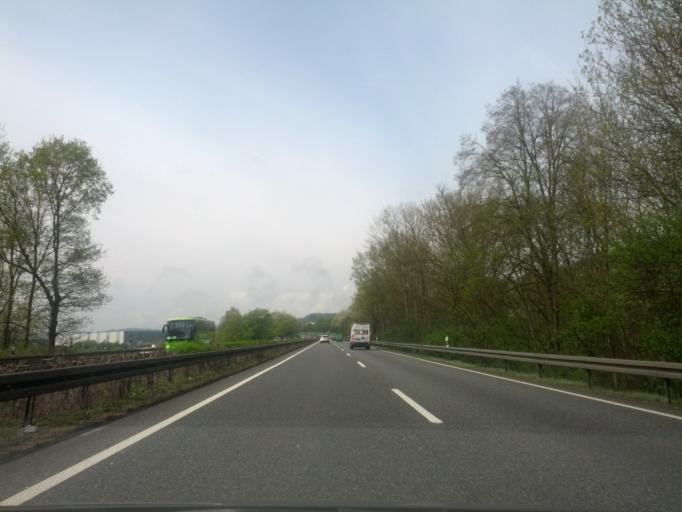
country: DE
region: Hesse
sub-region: Regierungsbezirk Kassel
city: Bad Hersfeld
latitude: 50.8509
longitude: 9.6890
